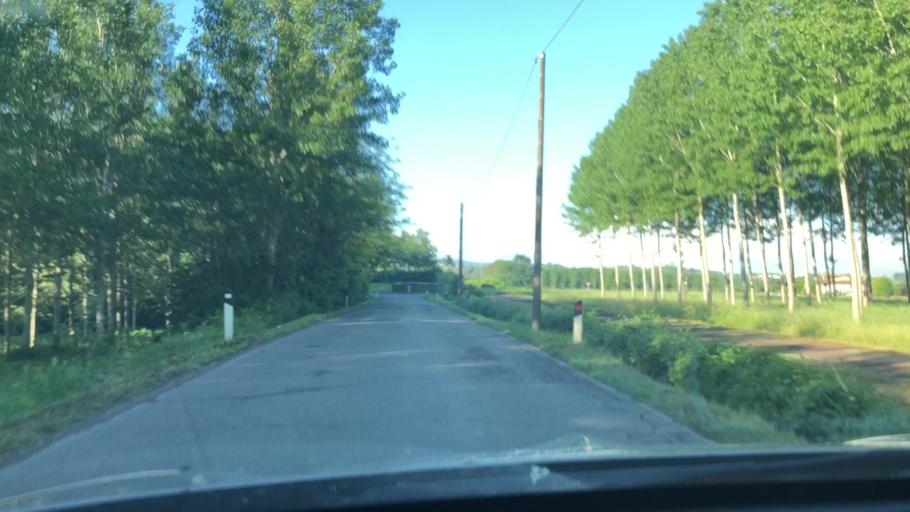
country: IT
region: Tuscany
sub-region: Province of Pisa
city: Forcoli
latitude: 43.6017
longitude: 10.6957
